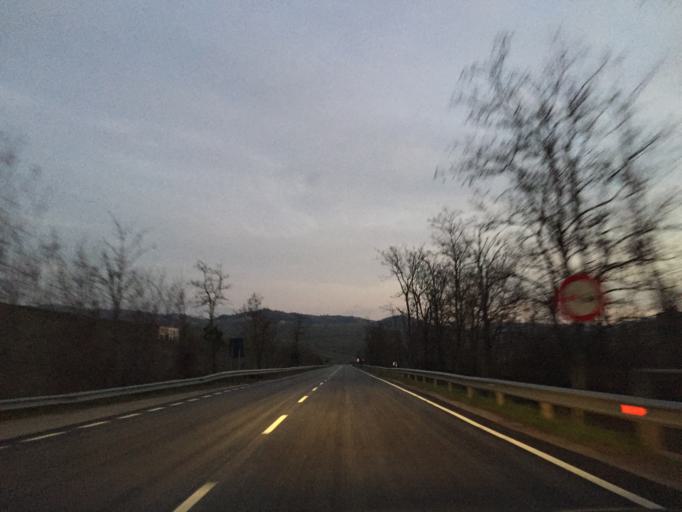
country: IT
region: Apulia
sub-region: Provincia di Foggia
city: Volturara Appula
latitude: 41.4651
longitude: 15.0574
